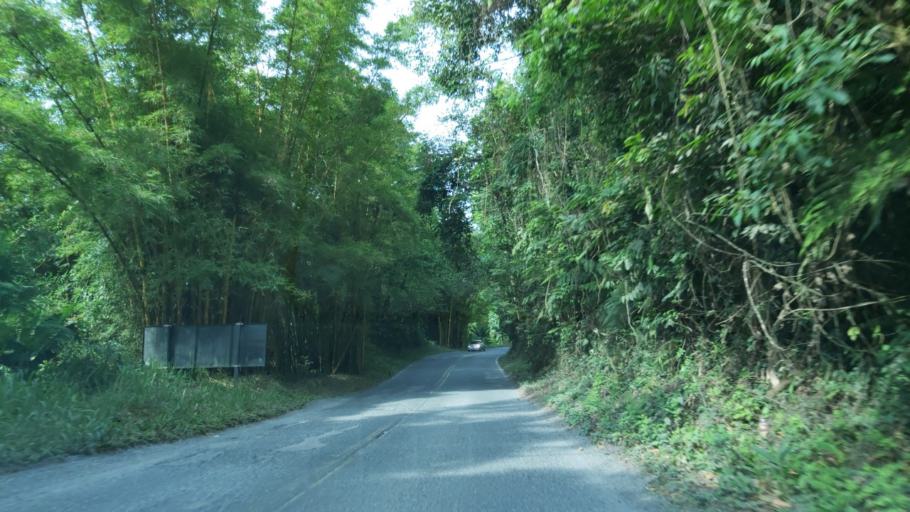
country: BR
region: Sao Paulo
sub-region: Juquia
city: Juquia
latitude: -24.1115
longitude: -47.6262
